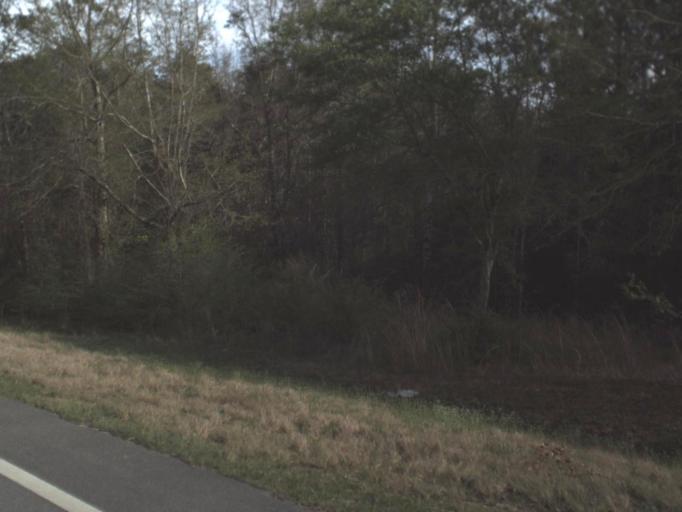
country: US
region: Florida
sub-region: Holmes County
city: Bonifay
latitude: 30.7889
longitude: -85.6946
